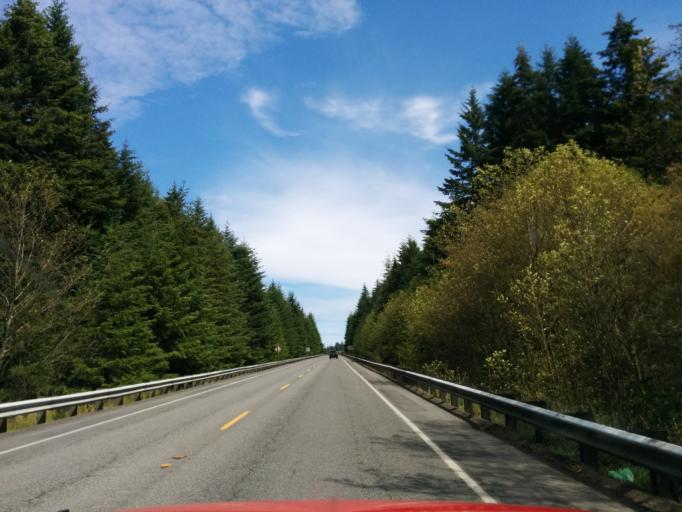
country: US
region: Washington
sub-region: Island County
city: Langley
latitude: 48.0022
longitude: -122.4233
